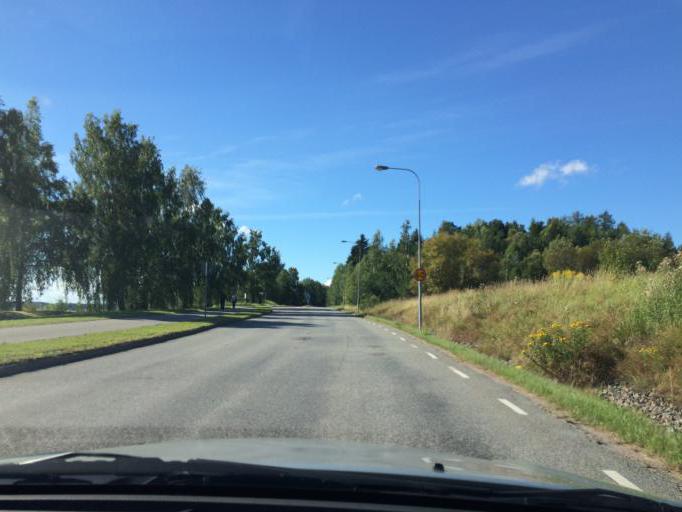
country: SE
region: Vaestmanland
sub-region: Vasteras
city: Vasteras
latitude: 59.6021
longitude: 16.6267
